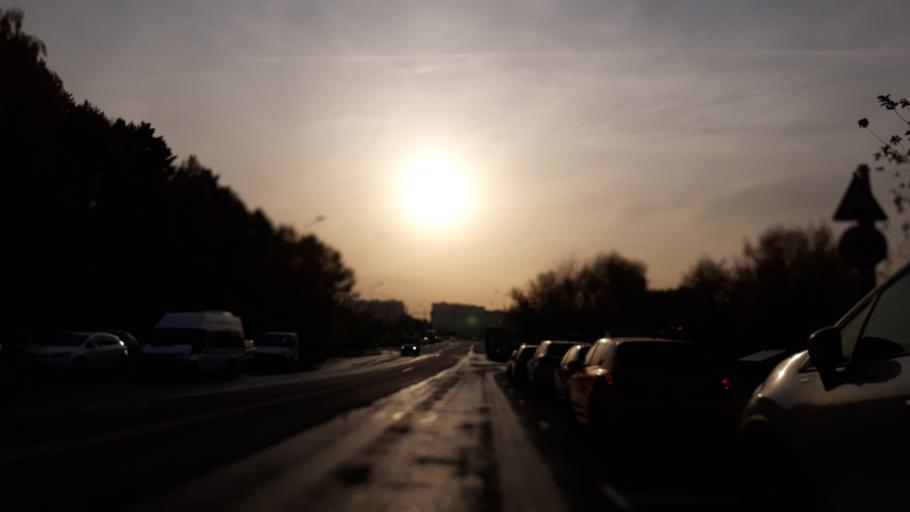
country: RU
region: Moscow
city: Zelenograd
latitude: 55.9920
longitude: 37.1721
